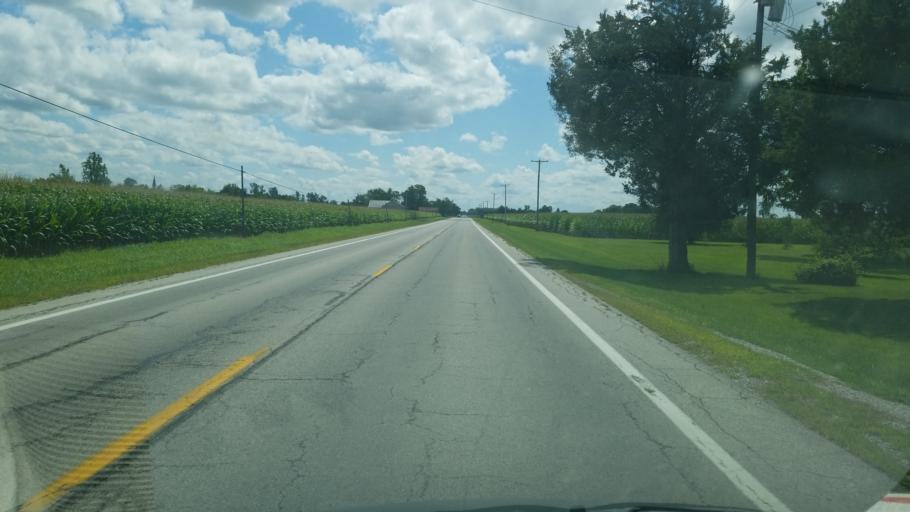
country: US
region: Ohio
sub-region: Henry County
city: Holgate
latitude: 41.3173
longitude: -84.1183
